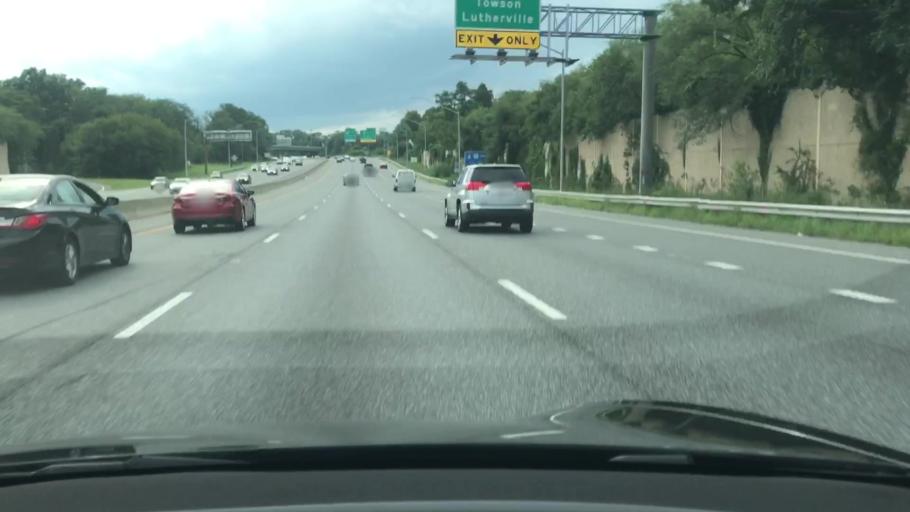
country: US
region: Maryland
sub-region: Baltimore County
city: Towson
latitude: 39.4139
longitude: -76.6053
